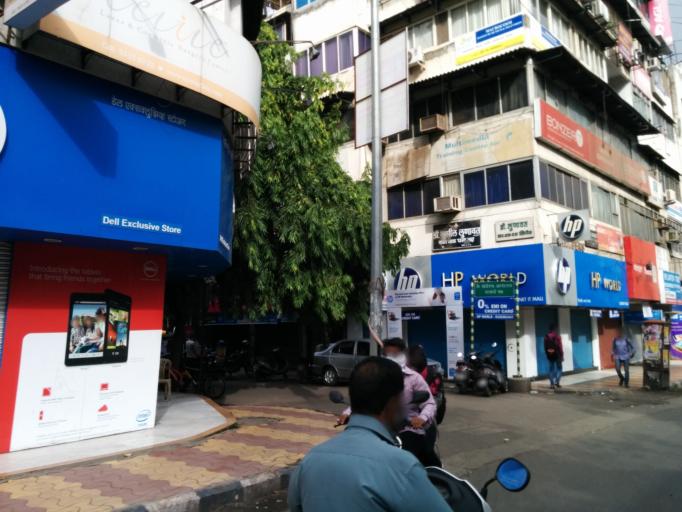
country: IN
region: Maharashtra
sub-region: Pune Division
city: Pune
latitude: 18.5097
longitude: 73.8472
